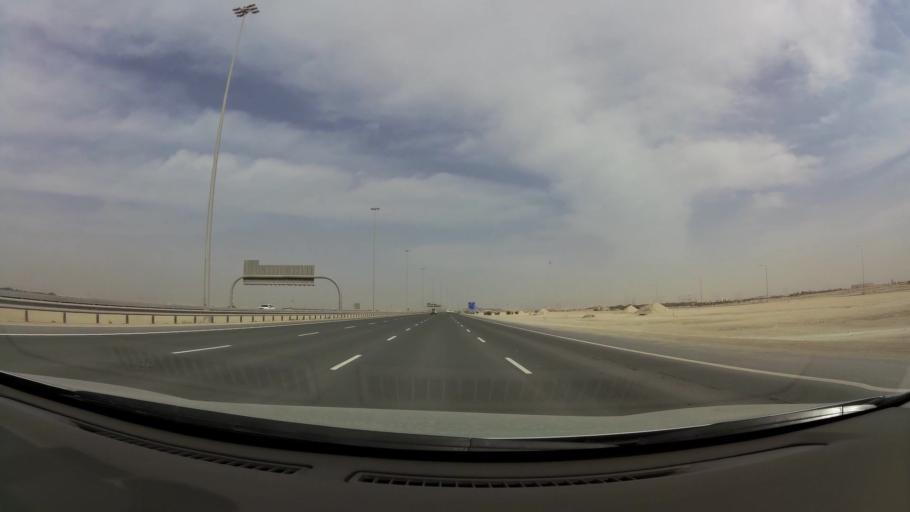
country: QA
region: Baladiyat ar Rayyan
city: Ash Shahaniyah
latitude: 25.3527
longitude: 51.2877
